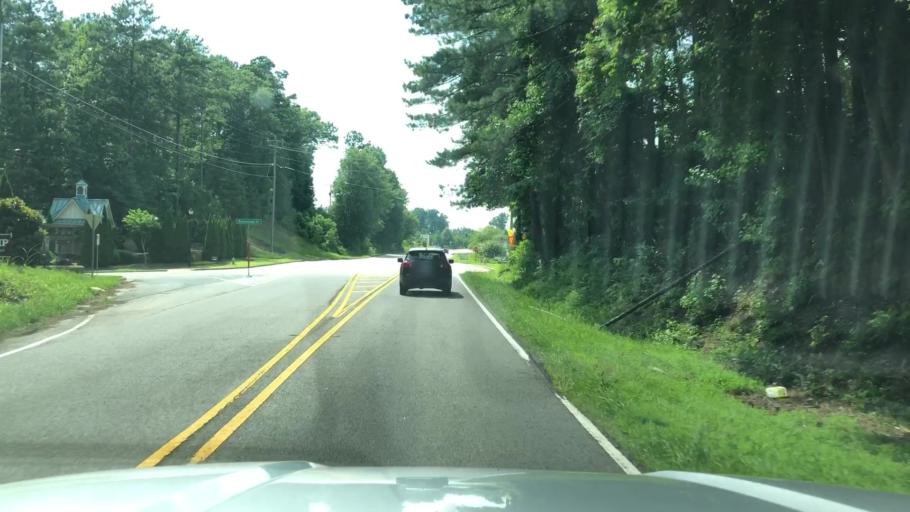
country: US
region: Georgia
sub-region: Paulding County
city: Dallas
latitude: 33.9552
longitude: -84.7832
